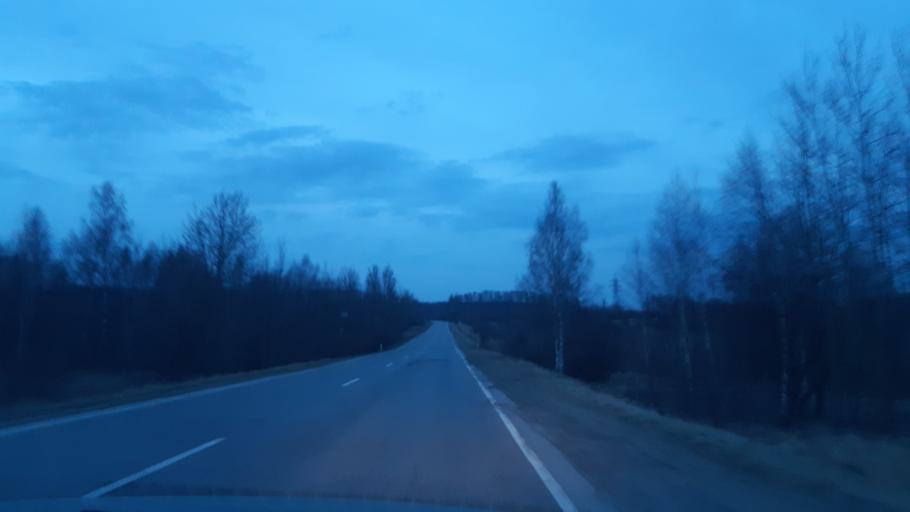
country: RU
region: Vladimir
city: Luknovo
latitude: 56.2171
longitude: 42.0312
